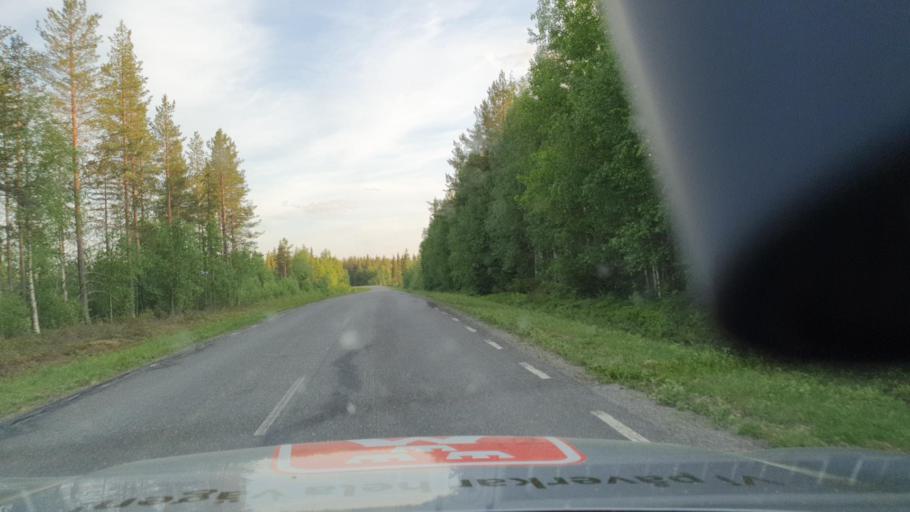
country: SE
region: Norrbotten
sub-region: Bodens Kommun
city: Boden
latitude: 66.2959
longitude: 21.3536
